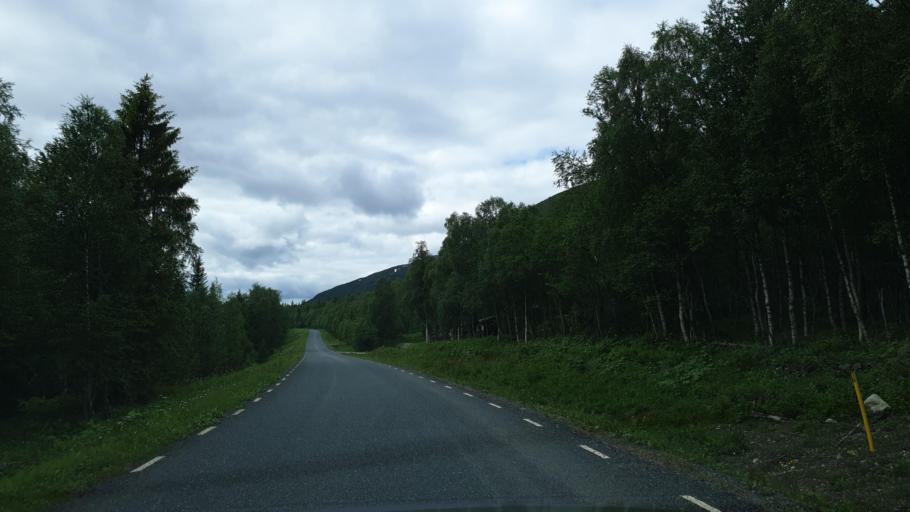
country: NO
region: Nordland
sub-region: Hattfjelldal
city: Hattfjelldal
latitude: 65.4381
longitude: 14.5680
